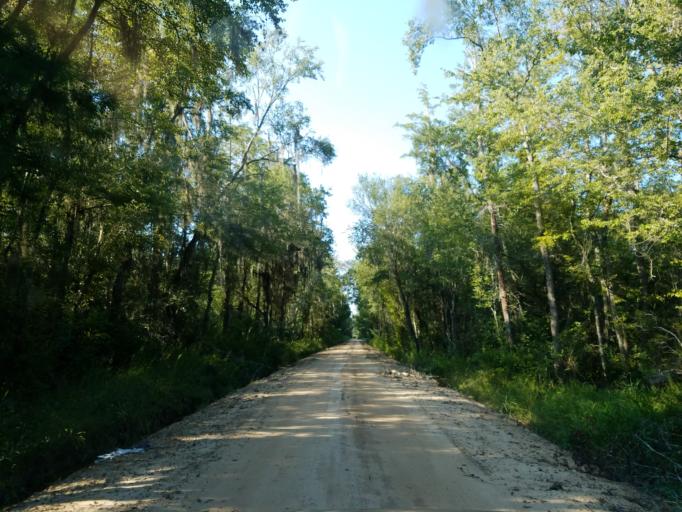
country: US
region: Georgia
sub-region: Lowndes County
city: Hahira
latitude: 31.0337
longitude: -83.3939
